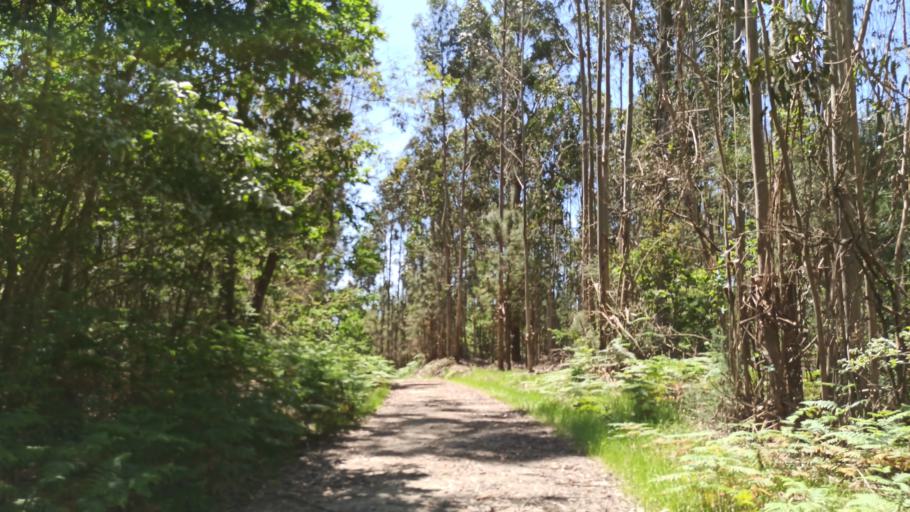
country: ES
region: Galicia
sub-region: Provincia da Coruna
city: Negreira
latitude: 42.9196
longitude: -8.7198
